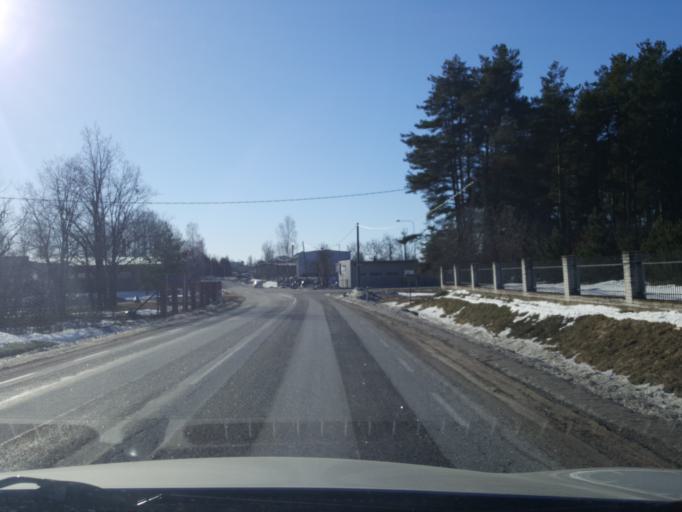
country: EE
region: Viljandimaa
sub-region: Viljandi linn
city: Viljandi
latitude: 58.3794
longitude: 25.6027
